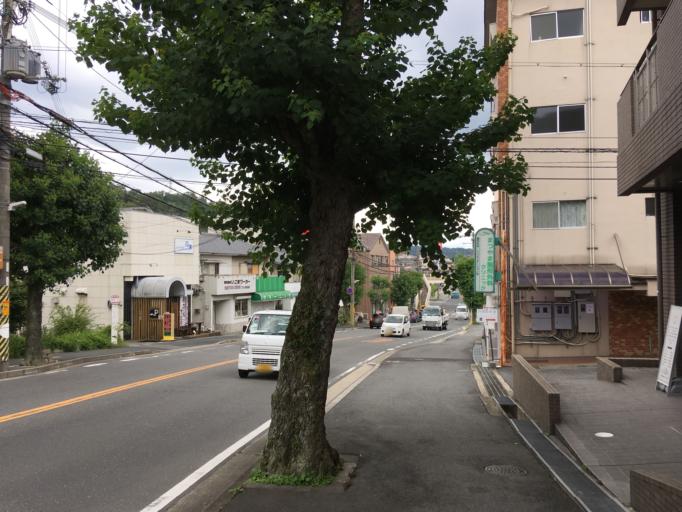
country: JP
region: Nara
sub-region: Ikoma-shi
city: Ikoma
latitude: 34.6872
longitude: 135.7155
